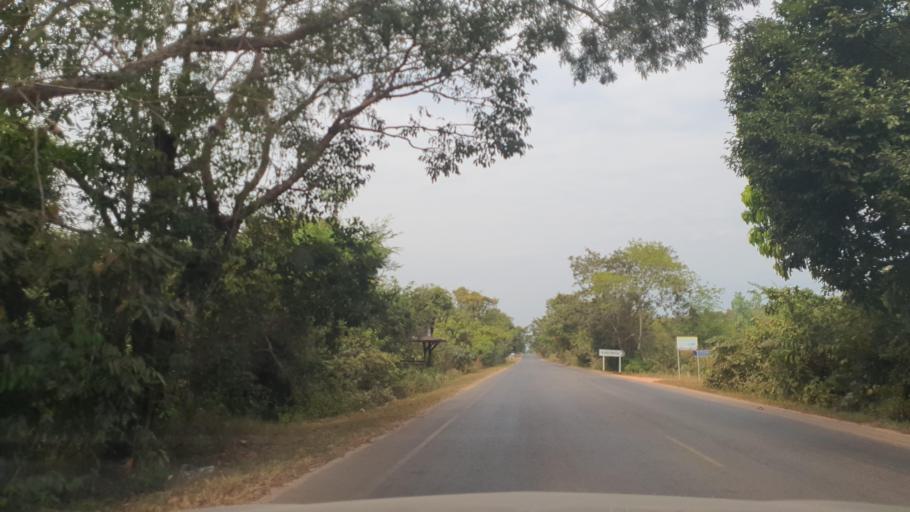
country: TH
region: Changwat Bueng Kan
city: Bung Khla
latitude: 18.2301
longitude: 104.0306
